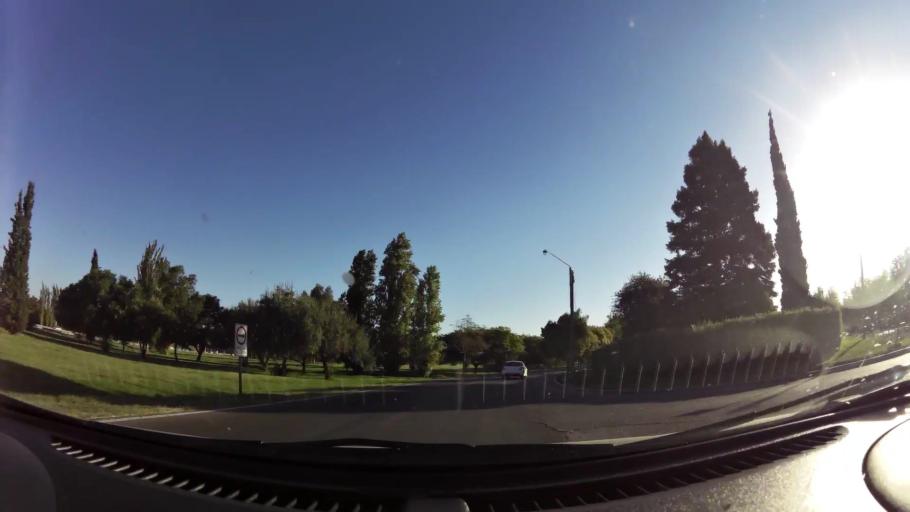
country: AR
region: San Juan
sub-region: Departamento de Santa Lucia
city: Santa Lucia
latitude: -31.5458
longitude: -68.5049
